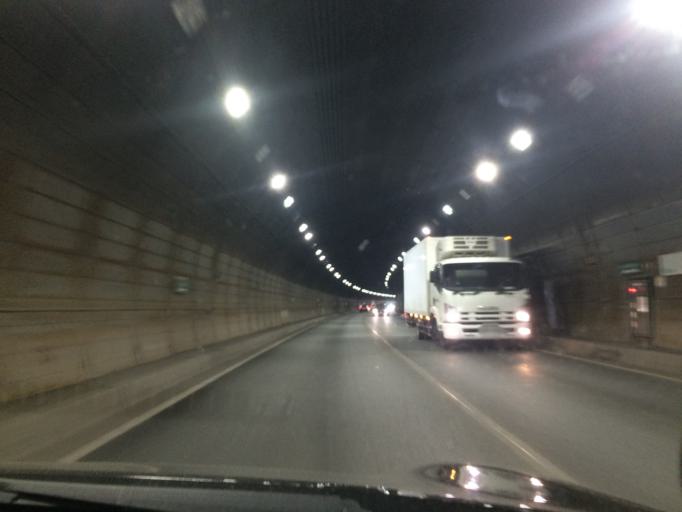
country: JP
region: Hokkaido
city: Fukagawa
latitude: 43.7300
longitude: 142.2001
